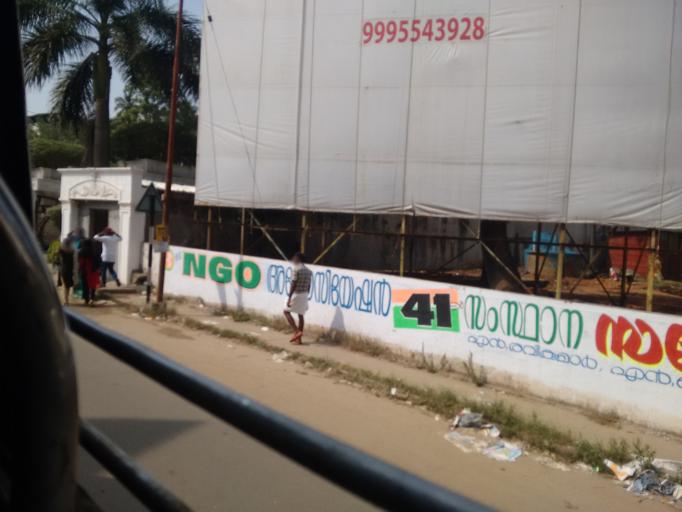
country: IN
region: Kerala
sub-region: Thrissur District
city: Trichur
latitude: 10.5142
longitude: 76.2132
